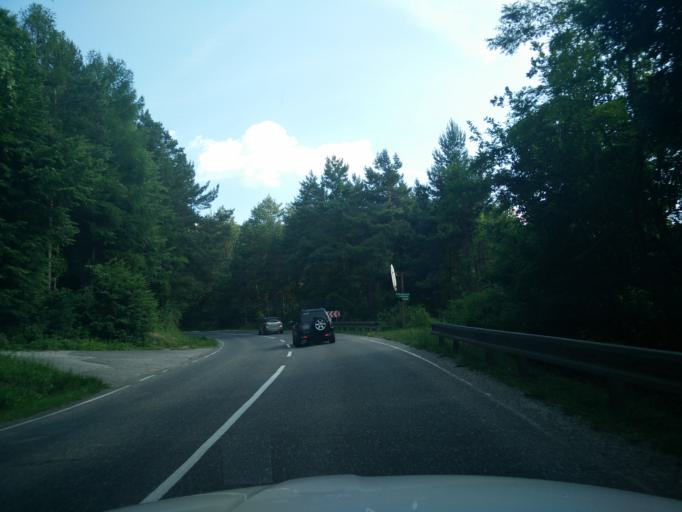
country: SK
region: Nitriansky
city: Prievidza
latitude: 48.8946
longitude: 18.7001
